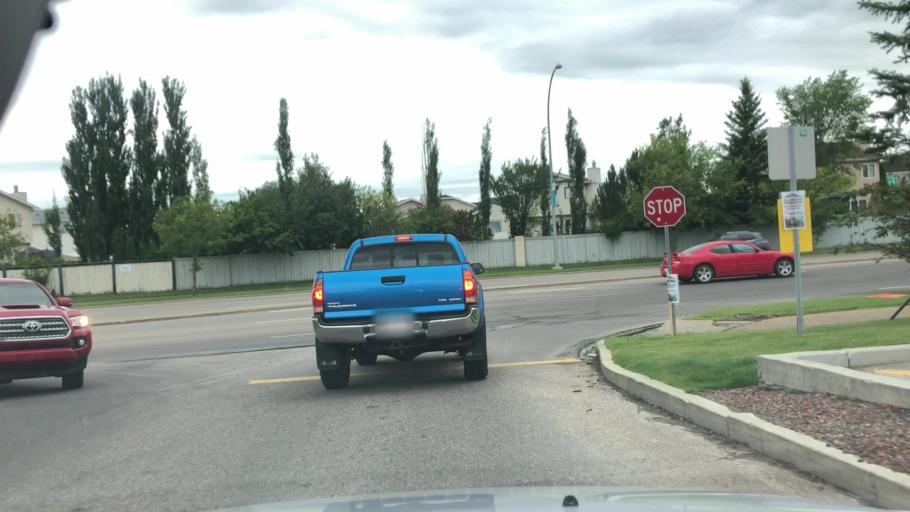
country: CA
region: Alberta
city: St. Albert
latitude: 53.6167
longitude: -113.5430
